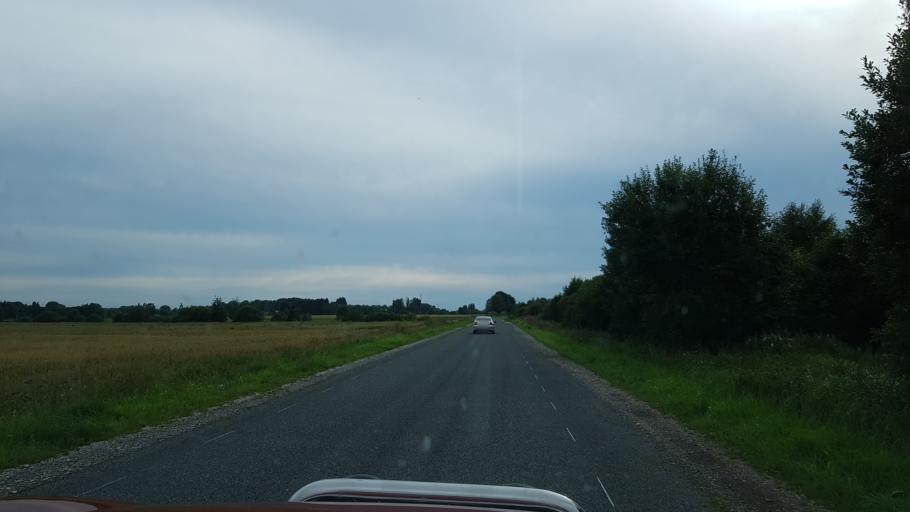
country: EE
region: Laeaene
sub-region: Lihula vald
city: Lihula
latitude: 58.8948
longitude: 23.8901
